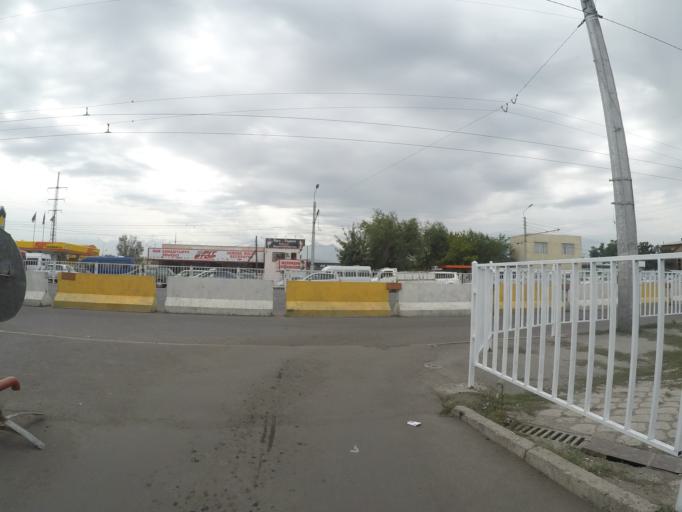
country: KG
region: Chuy
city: Bishkek
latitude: 42.8856
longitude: 74.5658
